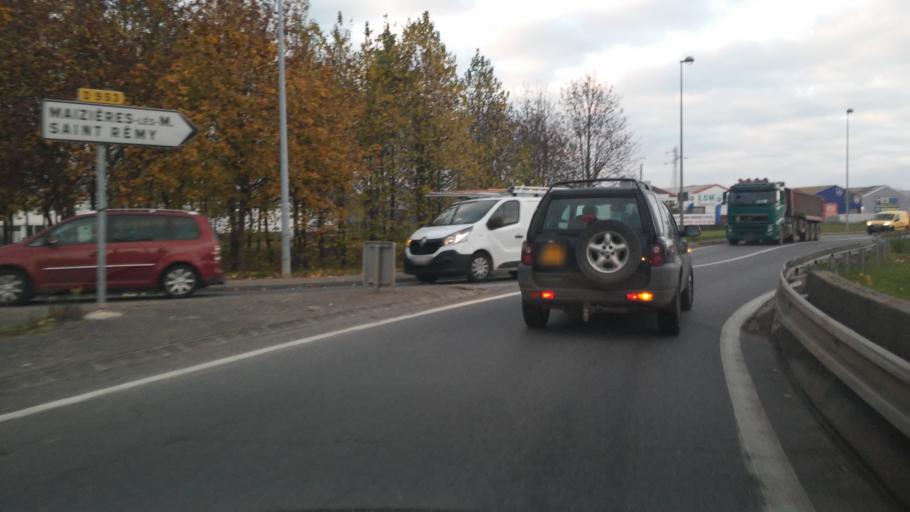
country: FR
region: Lorraine
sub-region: Departement de la Moselle
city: Woippy
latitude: 49.1575
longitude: 6.1589
